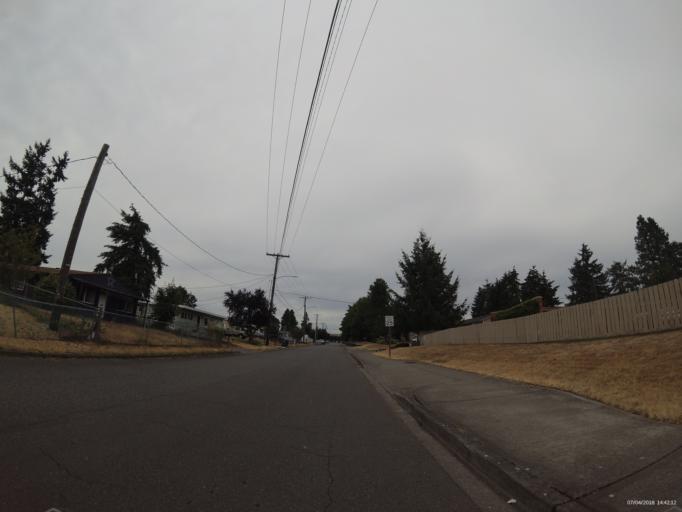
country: US
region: Washington
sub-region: Pierce County
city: Lakewood
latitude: 47.1637
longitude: -122.4995
